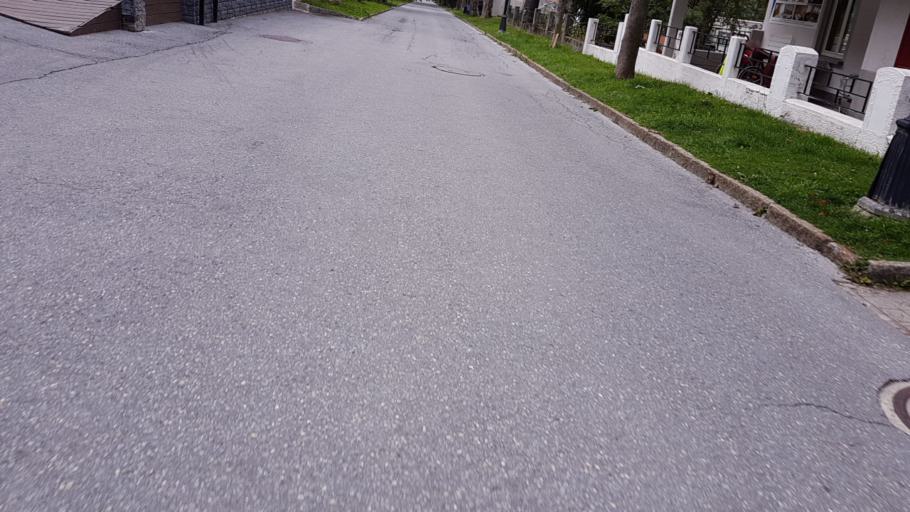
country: CH
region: Valais
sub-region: Leuk District
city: Leukerbad
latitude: 46.3773
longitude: 7.6299
